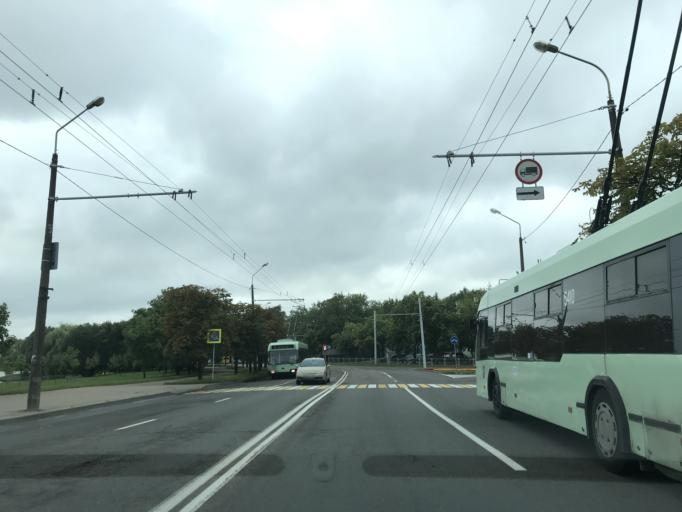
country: BY
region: Minsk
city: Borovlyany
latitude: 53.9479
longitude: 27.6412
